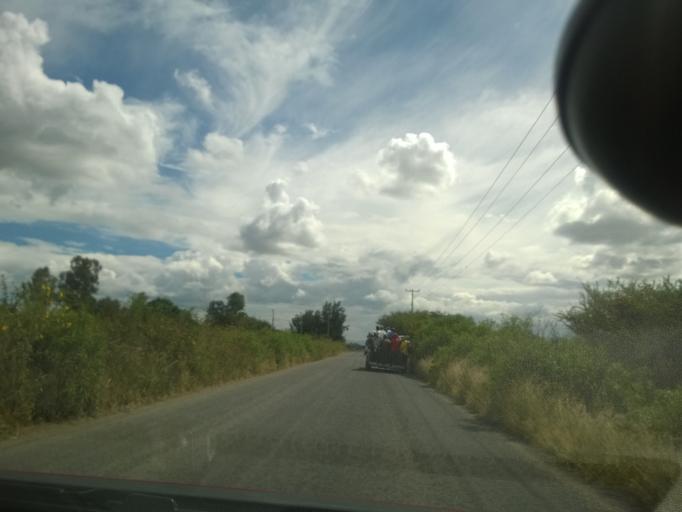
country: MX
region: Guanajuato
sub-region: Leon
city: El CERESO
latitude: 20.9761
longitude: -101.6530
